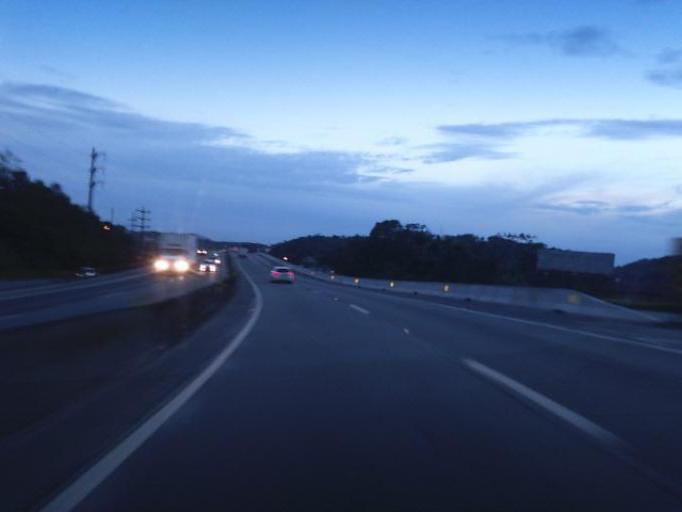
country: BR
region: Santa Catarina
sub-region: Joinville
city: Joinville
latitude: -26.3169
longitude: -48.8732
